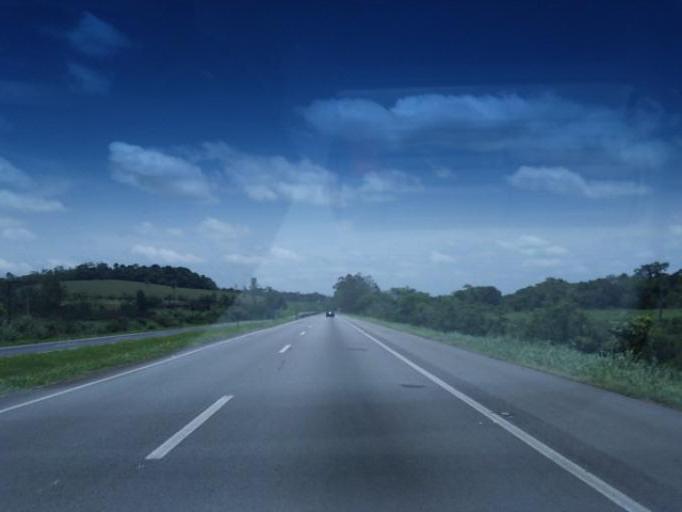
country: BR
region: Sao Paulo
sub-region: Registro
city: Registro
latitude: -24.4151
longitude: -47.7596
